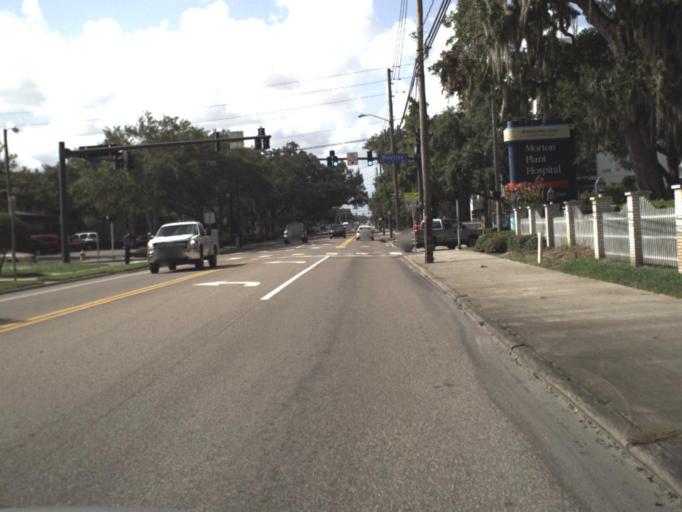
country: US
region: Florida
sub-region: Pinellas County
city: Clearwater
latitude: 27.9524
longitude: -82.8000
